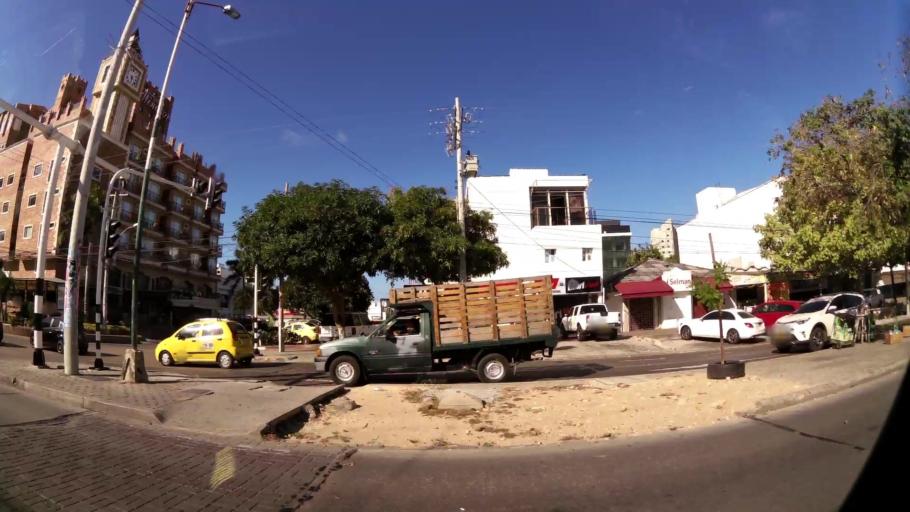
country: CO
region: Atlantico
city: Barranquilla
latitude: 11.0014
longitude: -74.8189
